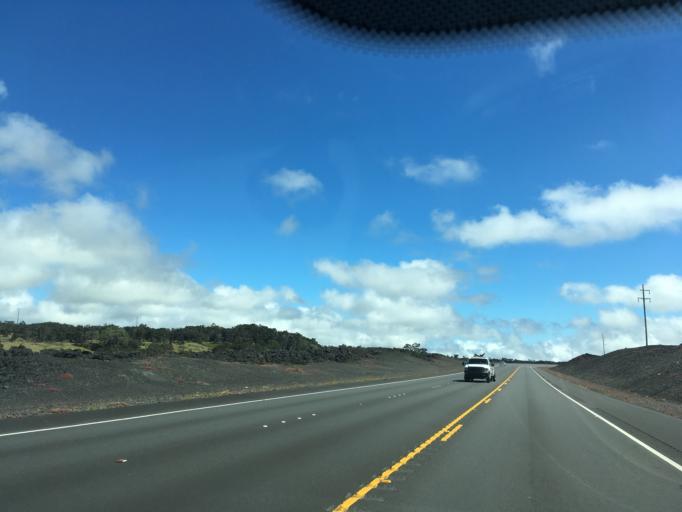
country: US
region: Hawaii
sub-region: Hawaii County
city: Volcano
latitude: 19.6816
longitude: -155.3974
